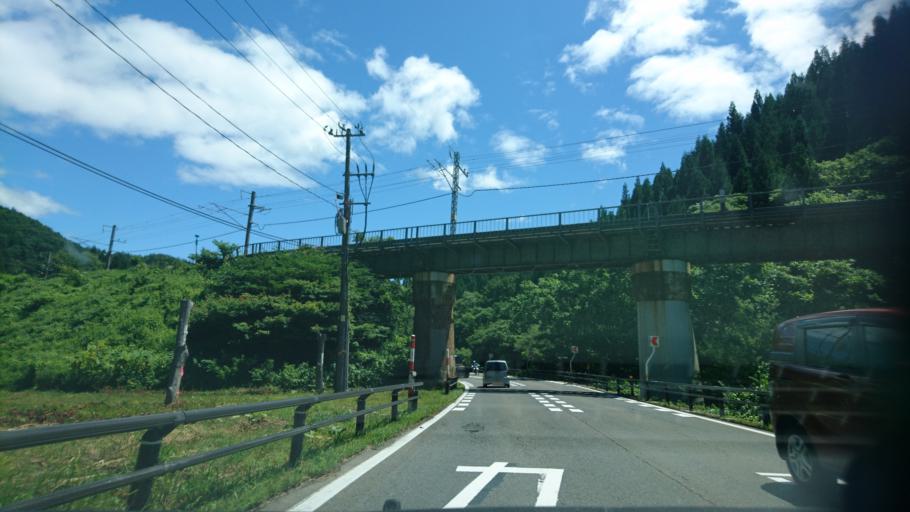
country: JP
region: Akita
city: Kakunodatemachi
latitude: 39.6600
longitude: 140.6729
